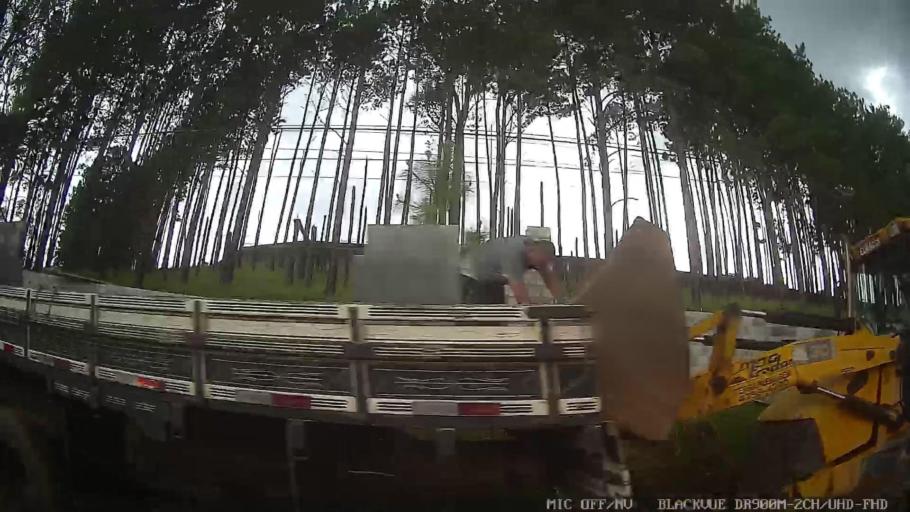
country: BR
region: Sao Paulo
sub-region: Suzano
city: Suzano
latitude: -23.5670
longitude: -46.3081
